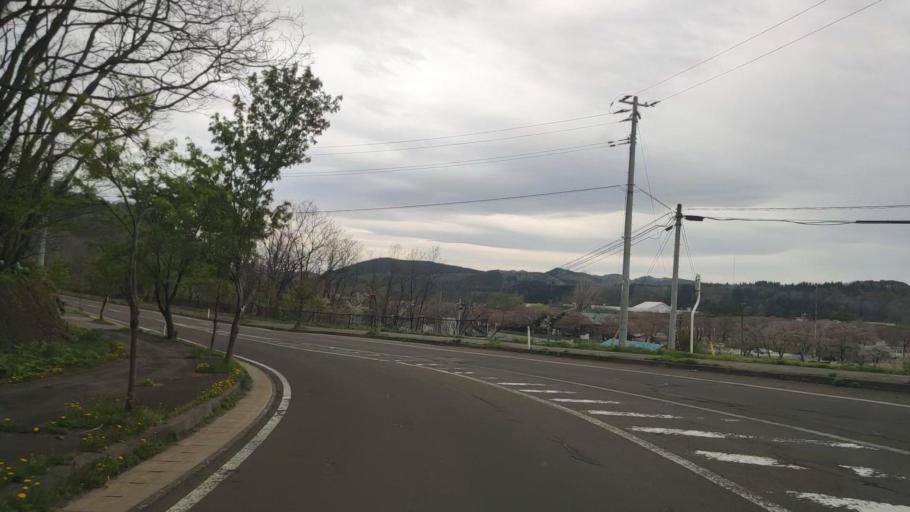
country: JP
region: Akita
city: Hanawa
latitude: 40.3293
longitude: 140.7472
